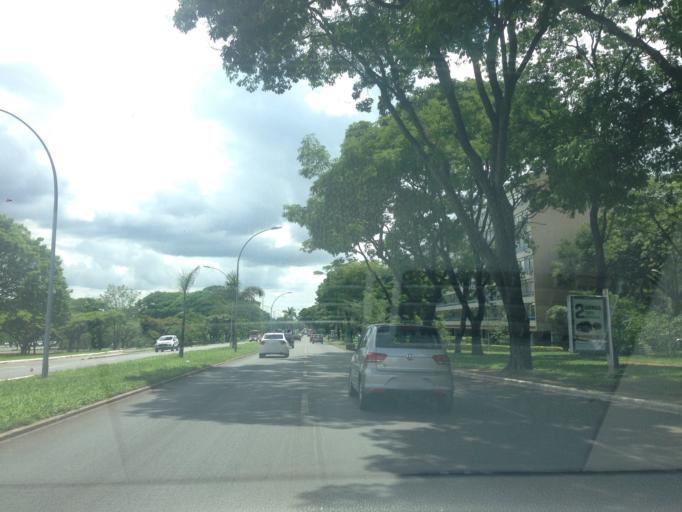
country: BR
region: Federal District
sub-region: Brasilia
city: Brasilia
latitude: -15.8228
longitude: -47.9101
